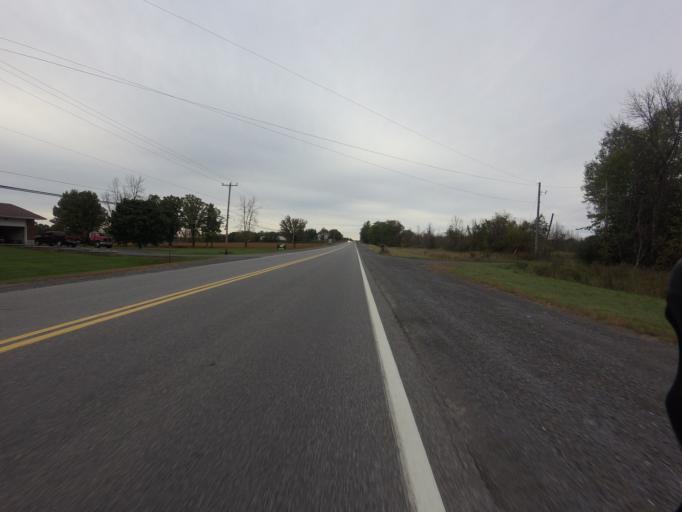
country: CA
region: Ontario
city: Bells Corners
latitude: 45.1446
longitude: -75.7131
